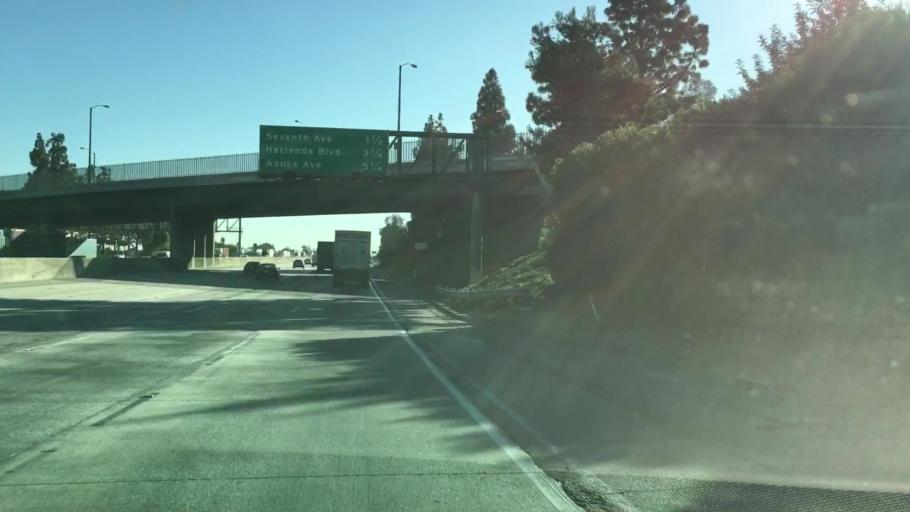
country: US
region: California
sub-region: Los Angeles County
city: Avocado Heights
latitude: 34.0289
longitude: -118.0139
